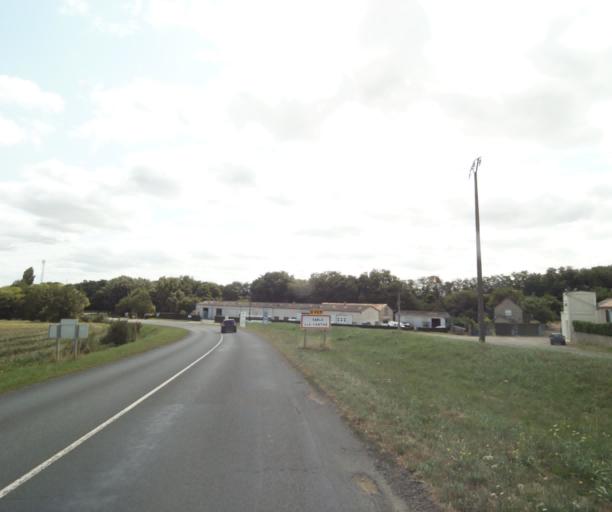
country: FR
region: Pays de la Loire
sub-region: Departement de la Sarthe
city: Sable-sur-Sarthe
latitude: 47.8402
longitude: -0.3528
